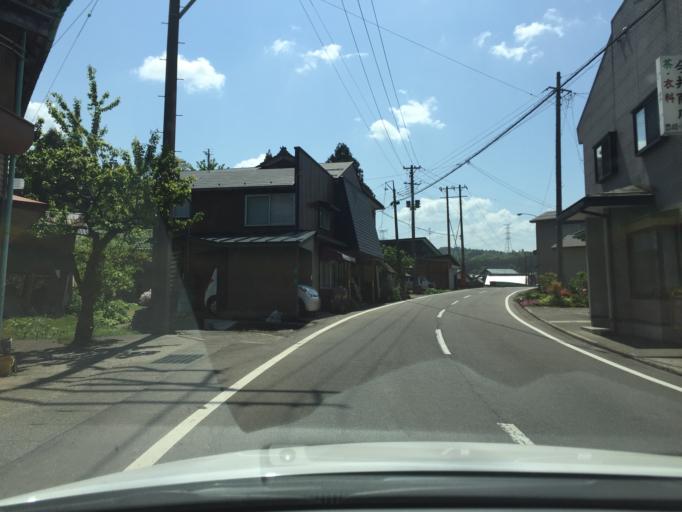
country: JP
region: Niigata
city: Tochio-honcho
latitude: 37.5470
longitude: 139.0899
